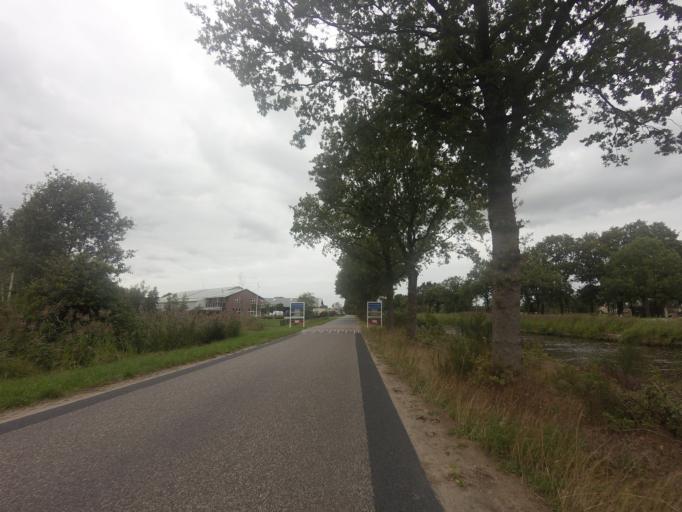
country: NL
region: Drenthe
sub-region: Gemeente Westerveld
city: Dwingeloo
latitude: 52.9811
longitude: 6.3115
